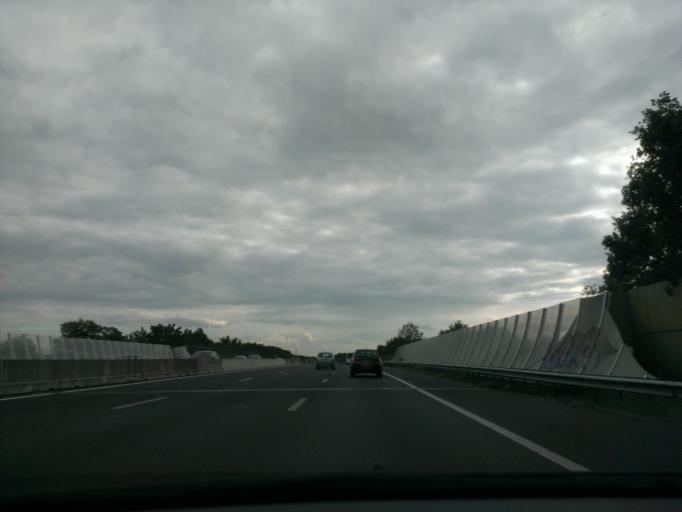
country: NL
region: Overijssel
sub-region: Gemeente Staphorst
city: Staphorst
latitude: 52.6440
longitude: 6.2018
